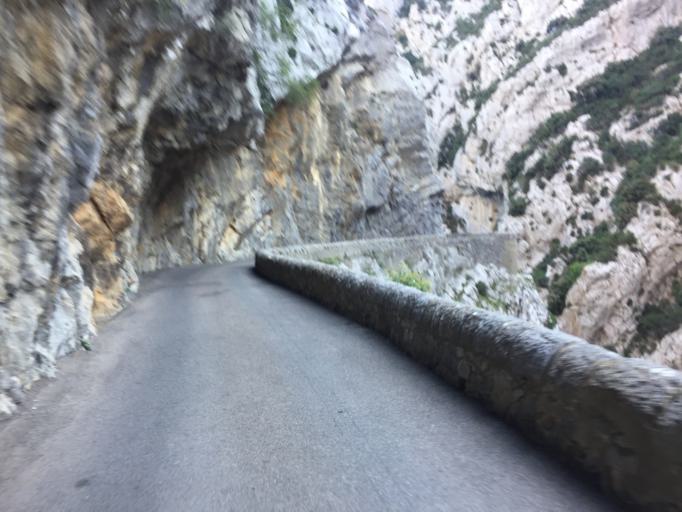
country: FR
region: Languedoc-Roussillon
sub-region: Departement des Pyrenees-Orientales
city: Saint-Paul-de-Fenouillet
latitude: 42.8415
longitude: 2.4798
